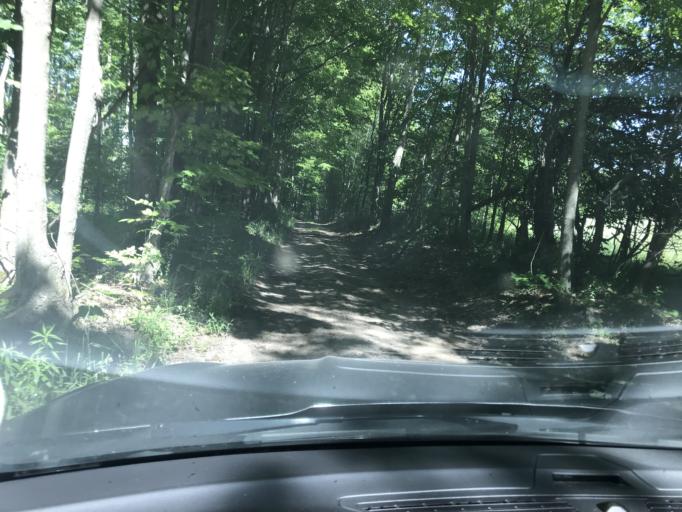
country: US
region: Michigan
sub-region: Cheboygan County
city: Cheboygan
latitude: 45.6072
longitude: -84.6704
